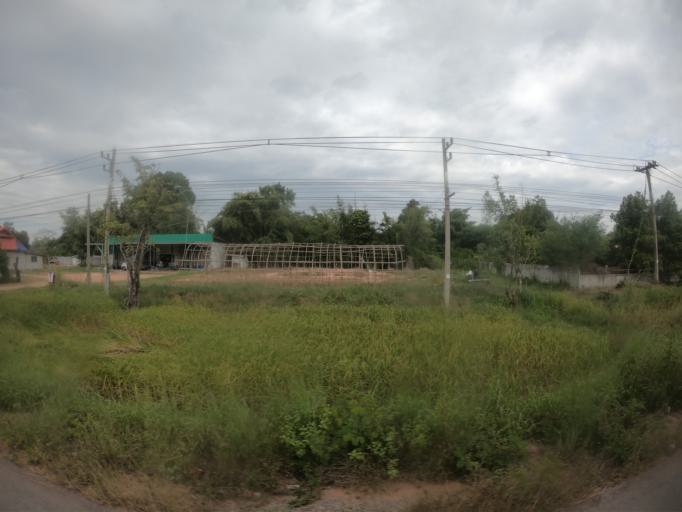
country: TH
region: Maha Sarakham
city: Kantharawichai
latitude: 16.3320
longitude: 103.2408
